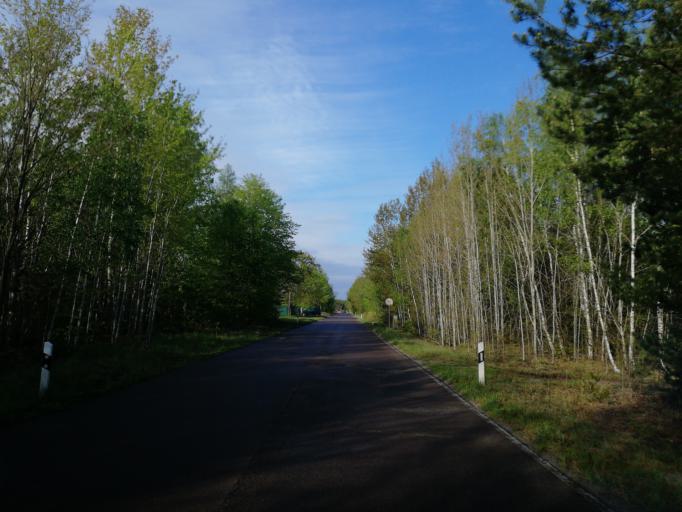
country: DE
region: Brandenburg
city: Lauchhammer
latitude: 51.5179
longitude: 13.7580
